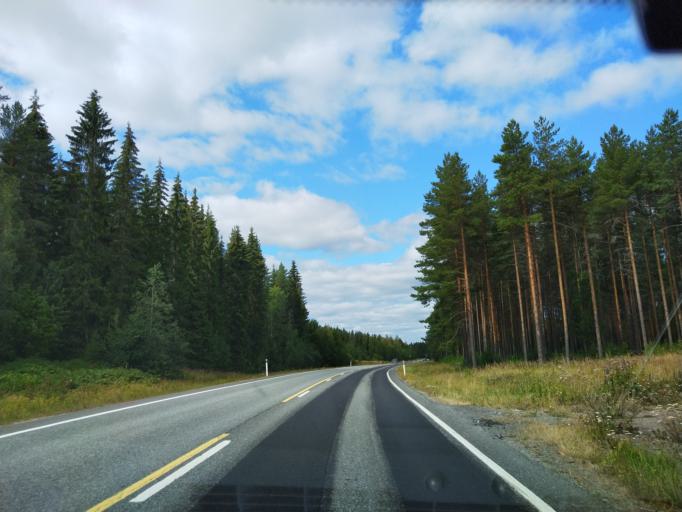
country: FI
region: Haeme
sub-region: Haemeenlinna
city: Tervakoski
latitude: 60.7418
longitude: 24.6748
